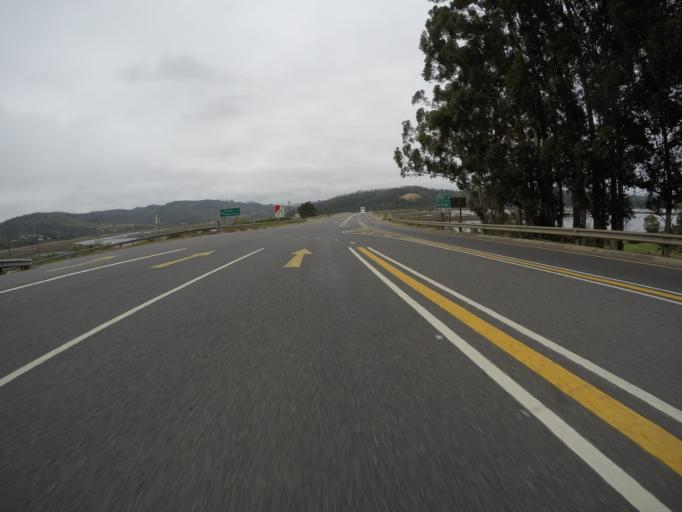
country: ZA
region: Western Cape
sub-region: Eden District Municipality
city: Knysna
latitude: -34.0328
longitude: 22.9905
